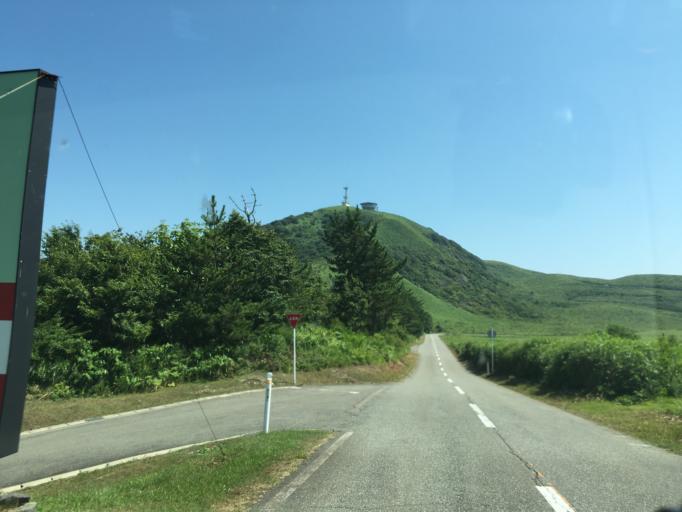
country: JP
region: Akita
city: Tenno
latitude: 39.9404
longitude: 139.8699
